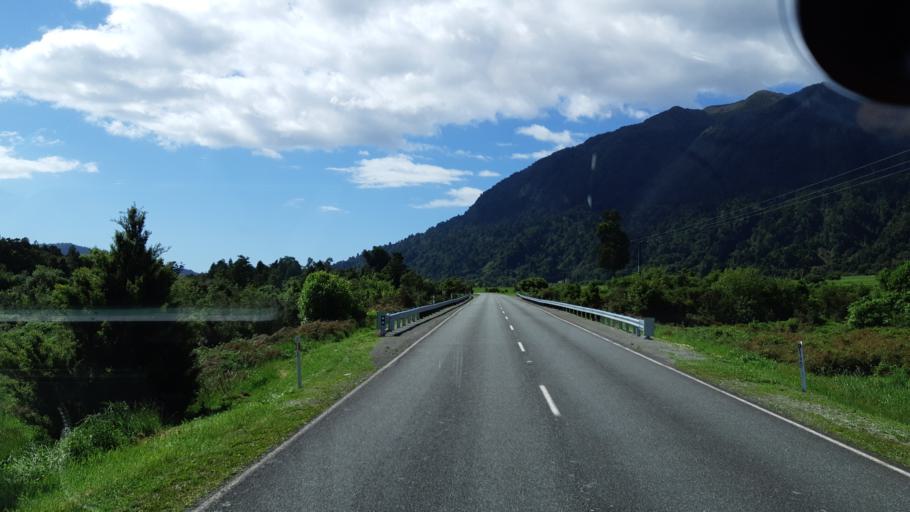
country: NZ
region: West Coast
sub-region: Westland District
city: Hokitika
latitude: -43.1159
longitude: 170.6337
